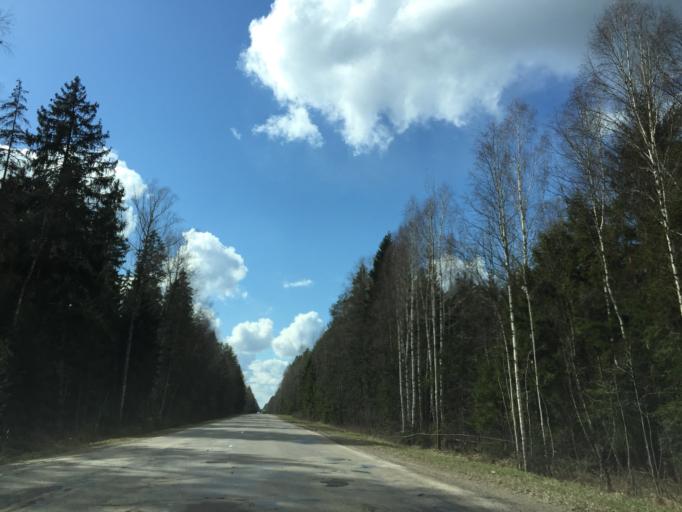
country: LV
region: Ikskile
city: Ikskile
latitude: 56.9486
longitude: 24.4902
